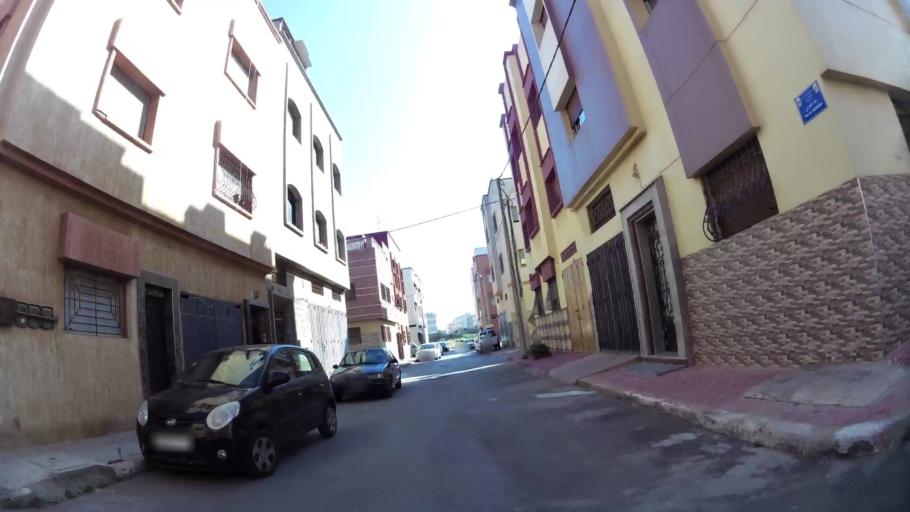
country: MA
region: Rabat-Sale-Zemmour-Zaer
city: Sale
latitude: 34.0626
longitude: -6.8085
